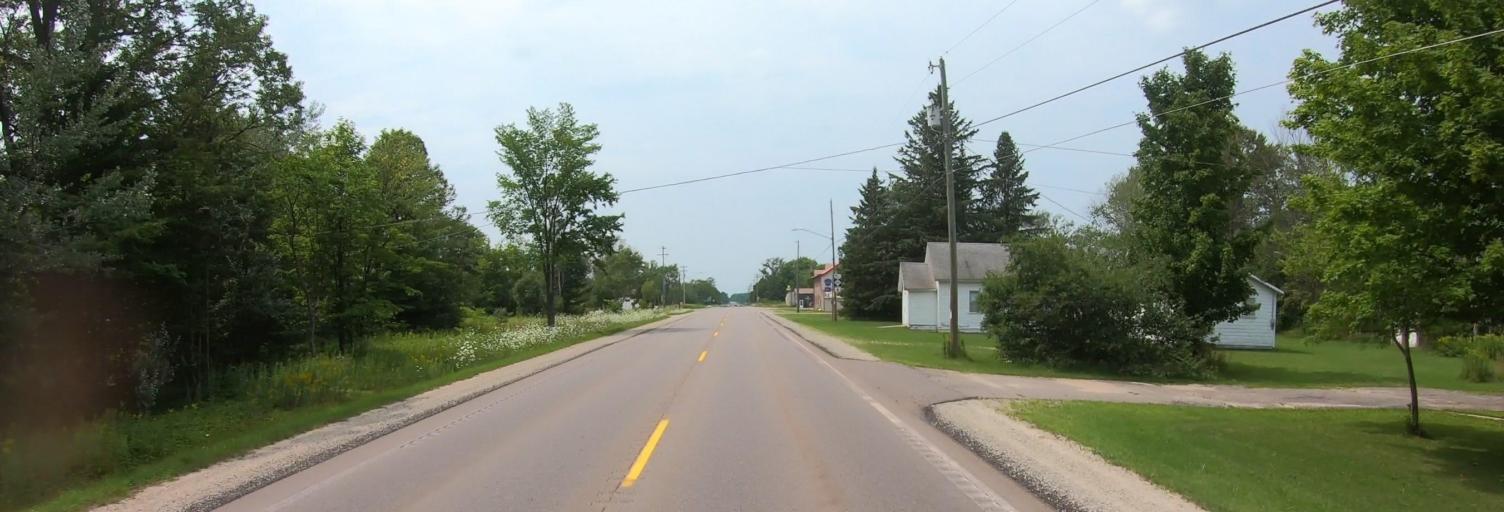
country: US
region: Michigan
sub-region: Alger County
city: Munising
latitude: 46.3549
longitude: -86.9687
